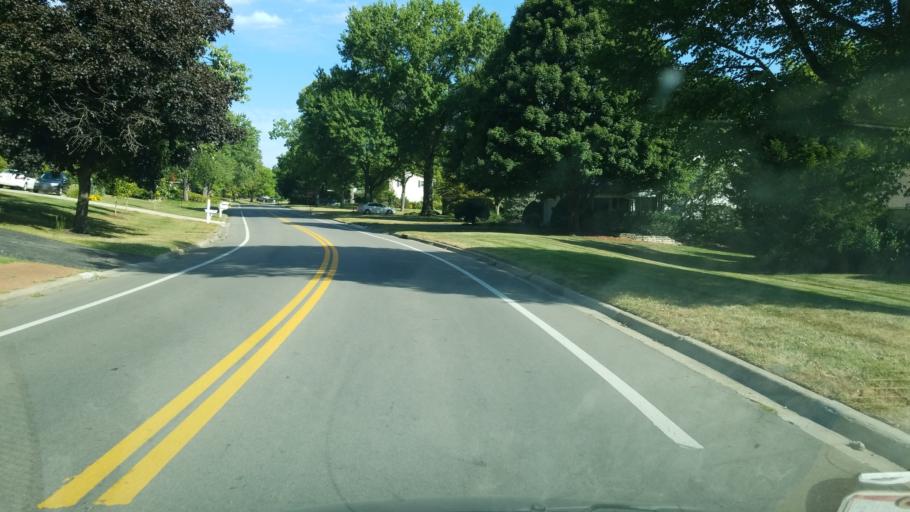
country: US
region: Ohio
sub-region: Franklin County
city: Worthington
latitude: 40.1276
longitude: -83.0427
